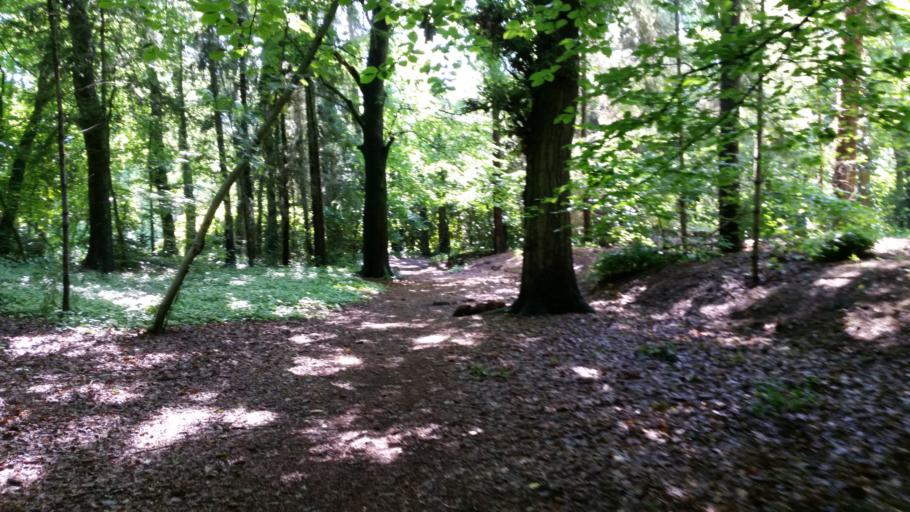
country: DE
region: Lower Saxony
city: Aurich
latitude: 53.4801
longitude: 7.4690
